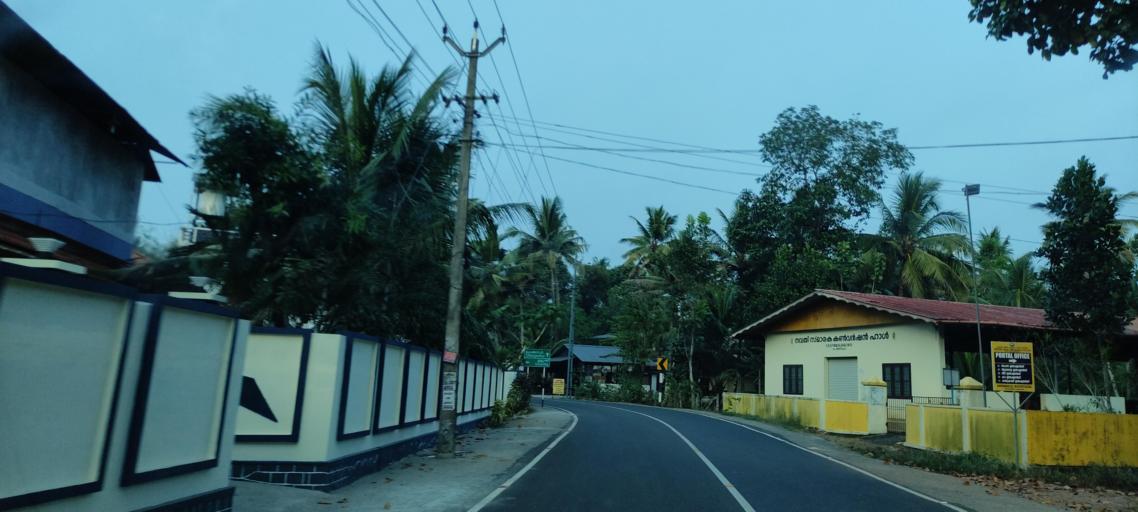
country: IN
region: Kerala
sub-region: Alappuzha
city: Mavelikara
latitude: 9.2724
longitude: 76.5580
